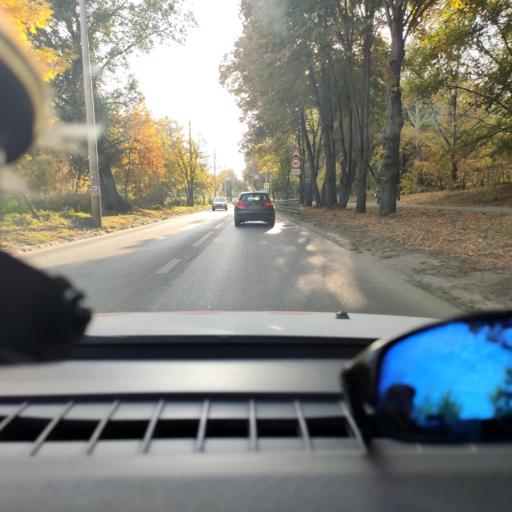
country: RU
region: Samara
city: Samara
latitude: 53.2285
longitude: 50.2183
